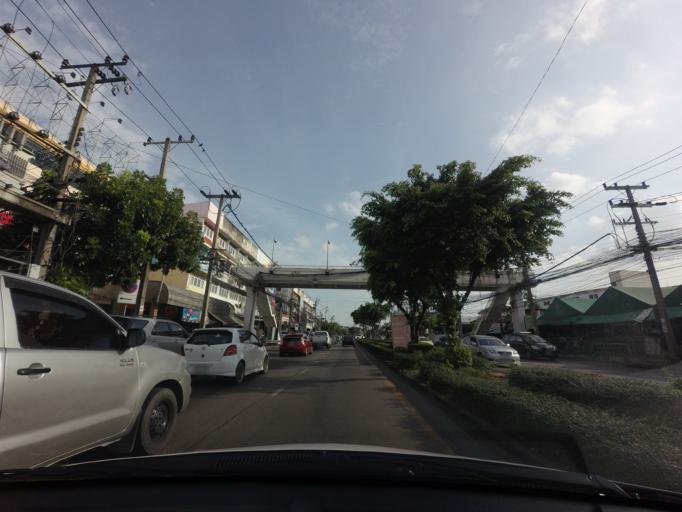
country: TH
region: Bangkok
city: Bueng Kum
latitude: 13.8092
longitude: 100.6499
